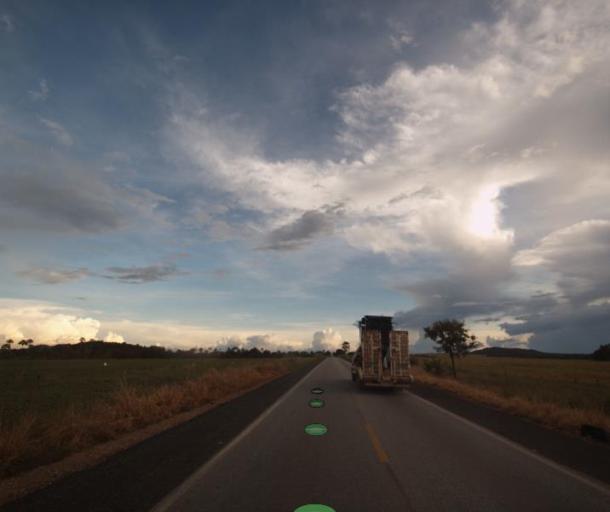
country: BR
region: Goias
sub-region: Uruacu
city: Uruacu
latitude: -14.0869
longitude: -49.0995
